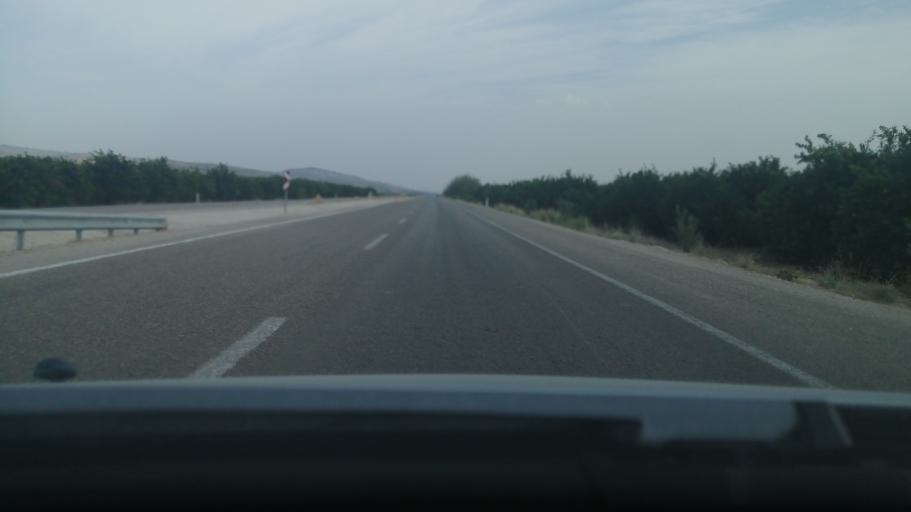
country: TR
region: Adana
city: Kozan
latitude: 37.3867
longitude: 35.8016
